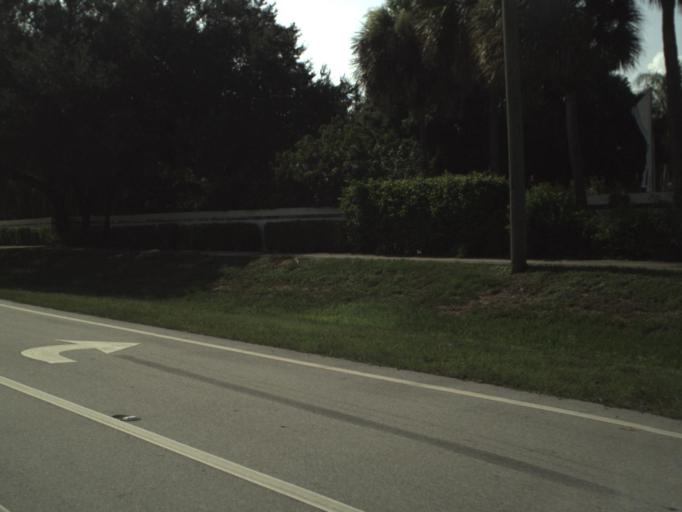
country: US
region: Florida
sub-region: Broward County
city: Coconut Creek
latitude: 26.2741
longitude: -80.1777
